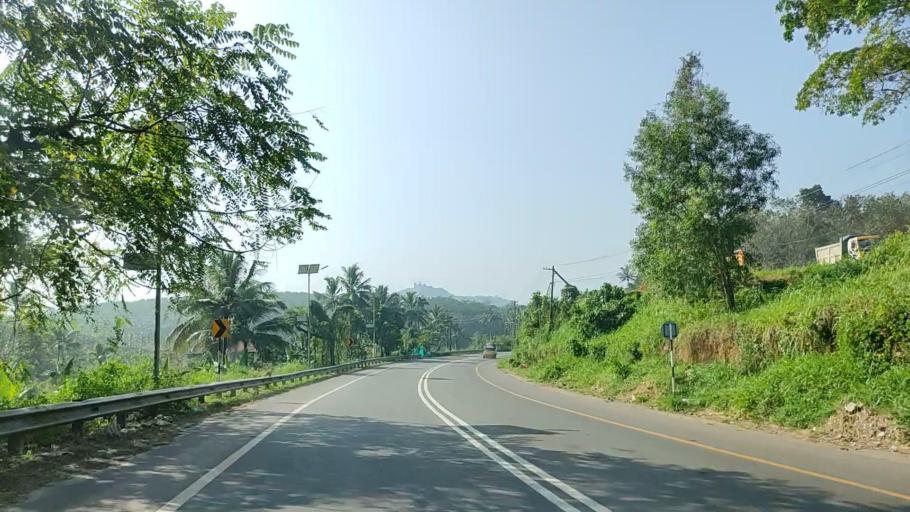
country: IN
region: Kerala
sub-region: Kollam
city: Punalur
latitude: 8.8840
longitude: 76.8694
